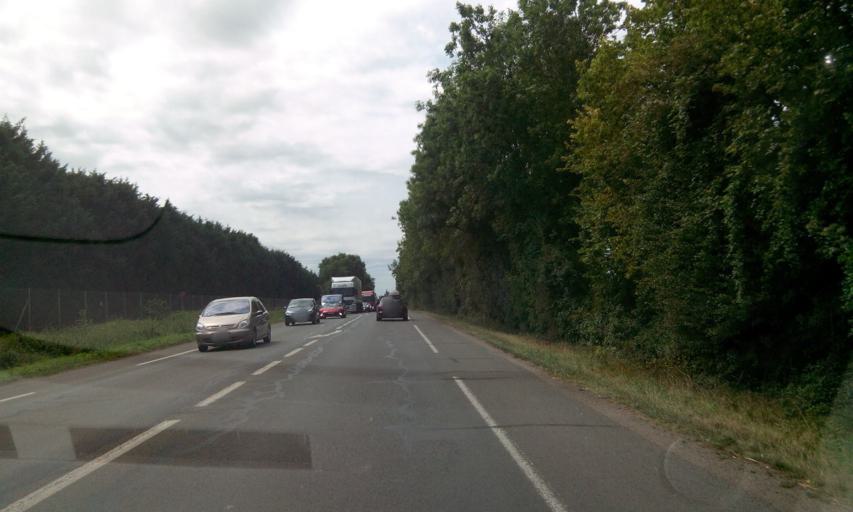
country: FR
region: Poitou-Charentes
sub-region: Departement des Deux-Sevres
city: Melle
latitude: 46.2187
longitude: -0.1378
